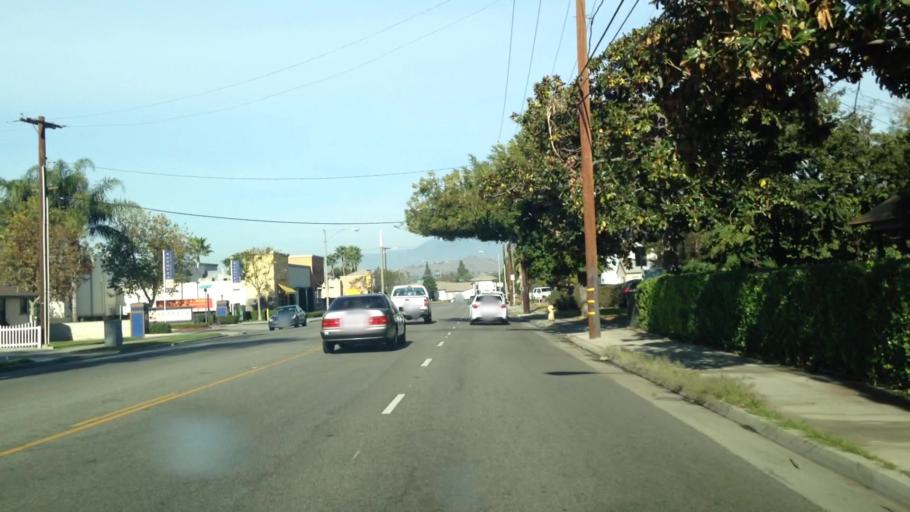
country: US
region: California
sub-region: Riverside County
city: Riverside
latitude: 33.9443
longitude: -117.4118
